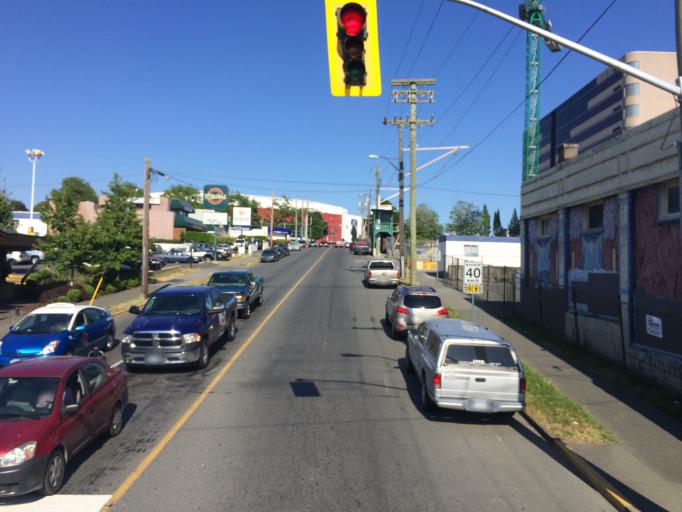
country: CA
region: British Columbia
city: Victoria
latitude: 48.4310
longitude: -123.3644
